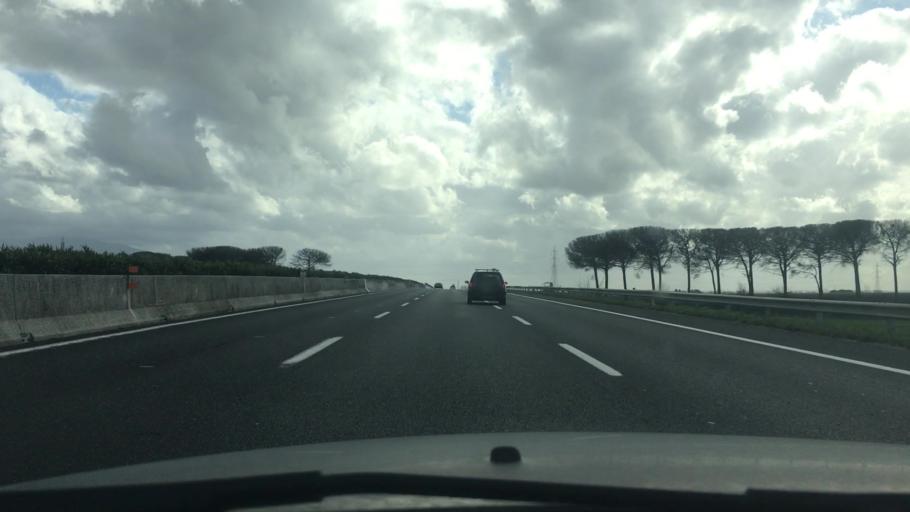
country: IT
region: Campania
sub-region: Provincia di Napoli
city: Pascarola
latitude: 40.9883
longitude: 14.3250
